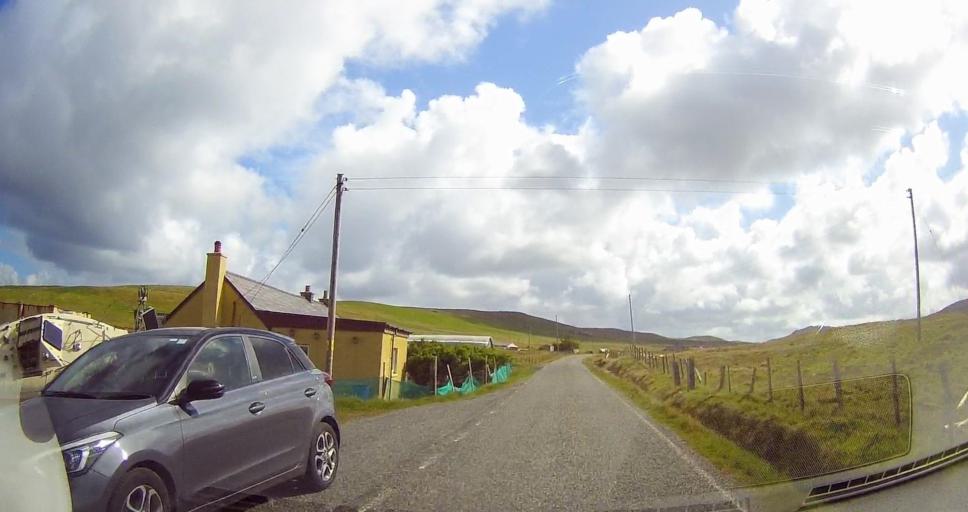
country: GB
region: Scotland
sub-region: Shetland Islands
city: Lerwick
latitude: 60.5768
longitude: -1.3314
